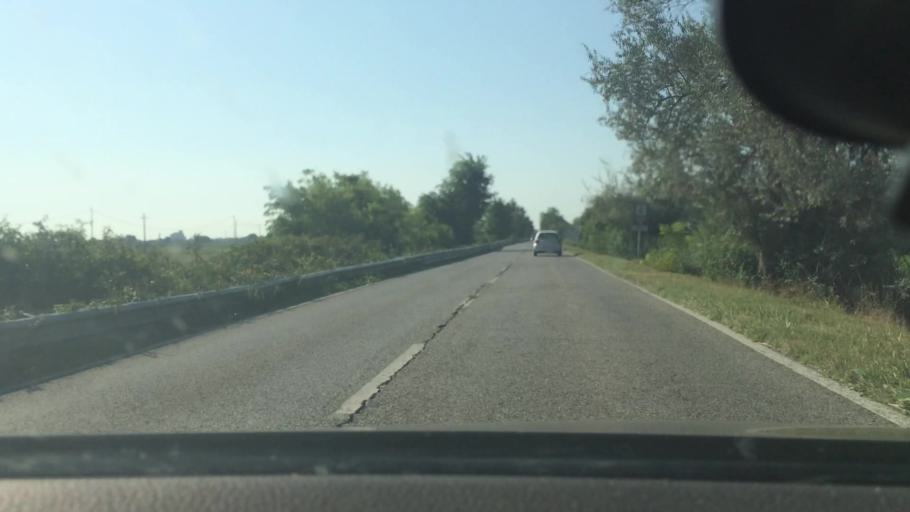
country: IT
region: Emilia-Romagna
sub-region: Provincia di Ferrara
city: Comacchio
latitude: 44.7101
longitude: 12.1613
